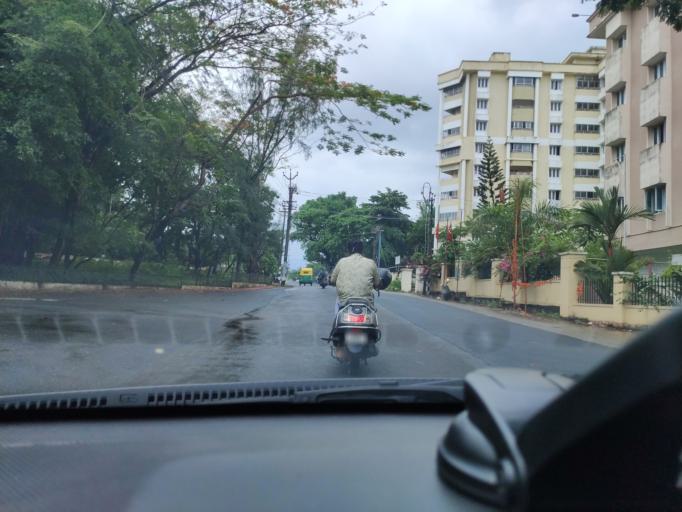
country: IN
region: Kerala
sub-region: Ernakulam
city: Elur
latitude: 10.0240
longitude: 76.3329
